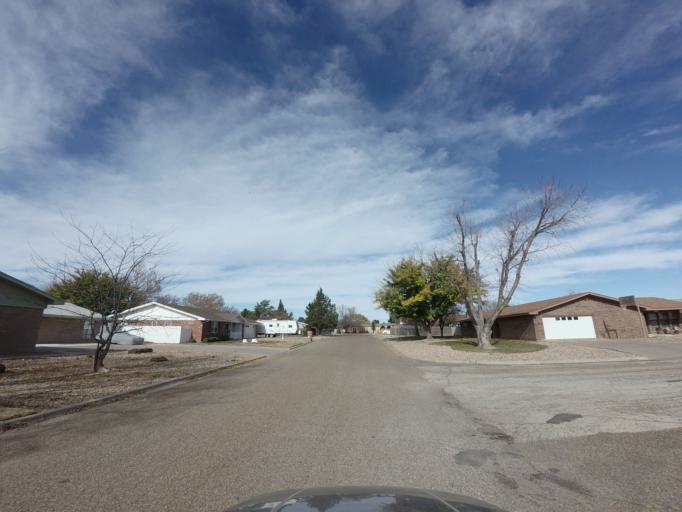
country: US
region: New Mexico
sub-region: Curry County
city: Clovis
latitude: 34.4149
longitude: -103.1857
